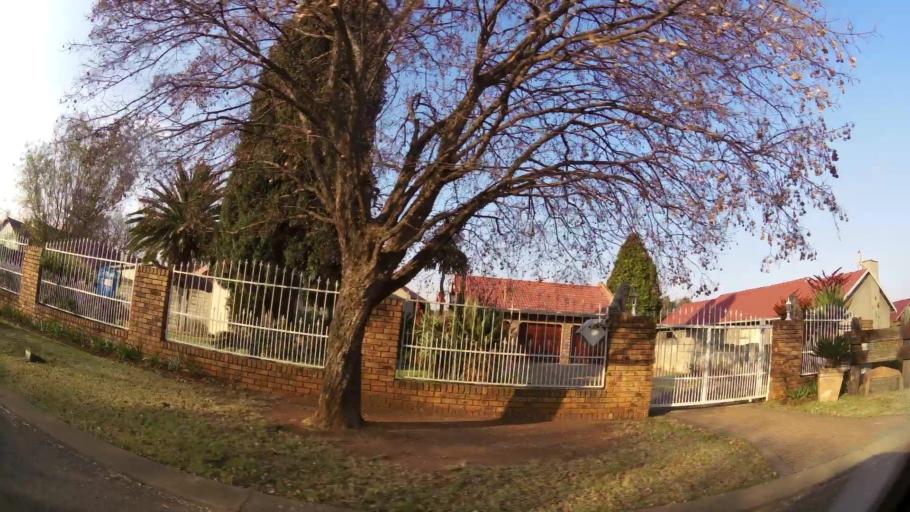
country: ZA
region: Gauteng
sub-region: Ekurhuleni Metropolitan Municipality
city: Springs
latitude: -26.2558
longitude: 28.3979
